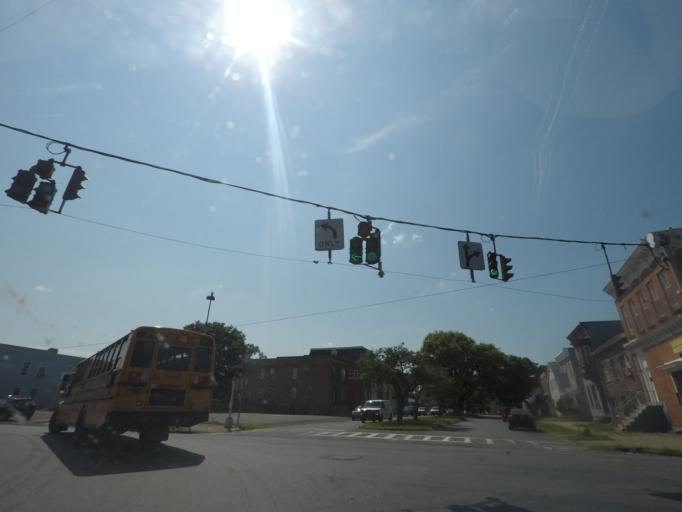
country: US
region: New York
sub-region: Albany County
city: Watervliet
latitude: 42.7328
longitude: -73.7010
